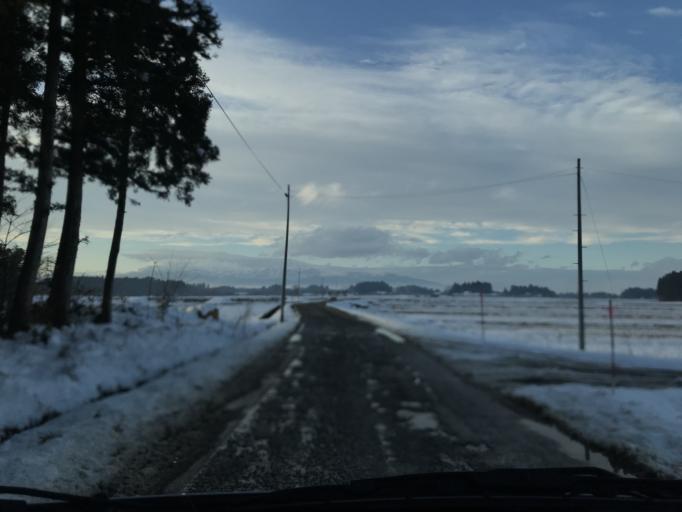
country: JP
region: Iwate
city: Mizusawa
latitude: 39.0561
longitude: 141.0928
